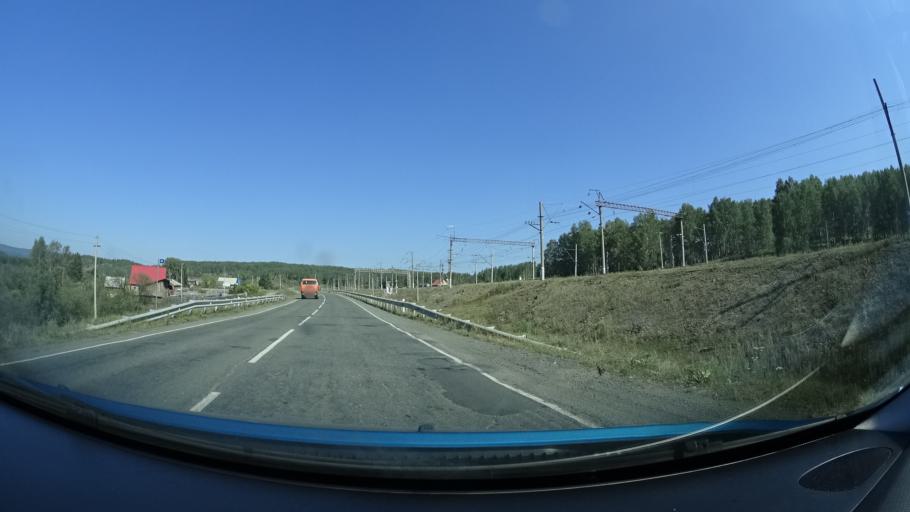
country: RU
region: Bashkortostan
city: Abzakovo
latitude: 53.8154
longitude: 58.6420
